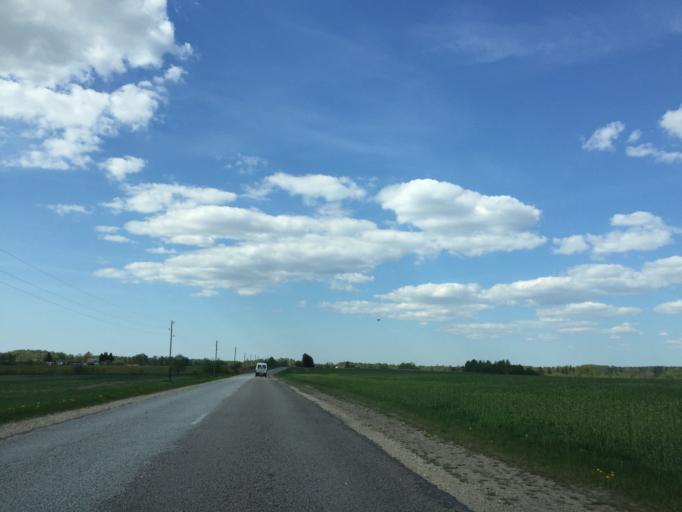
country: LV
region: Limbazu Rajons
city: Limbazi
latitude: 57.4542
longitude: 24.7236
